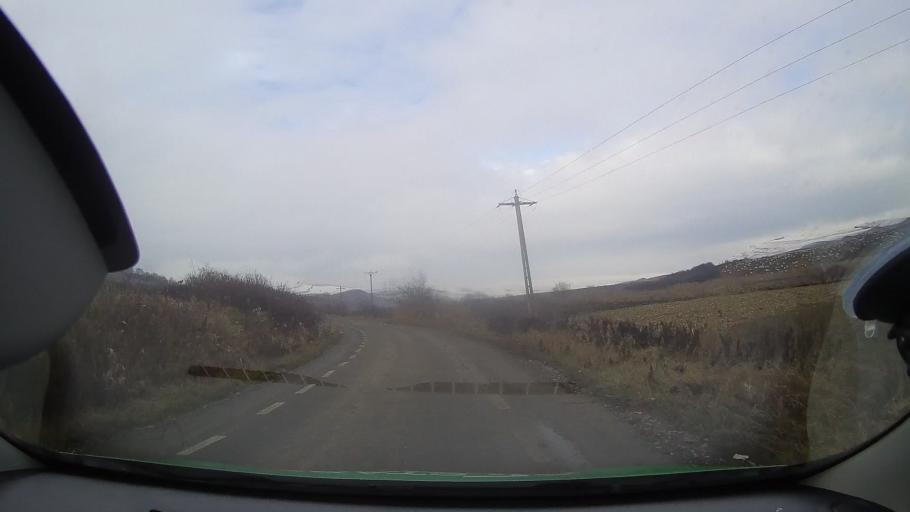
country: RO
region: Mures
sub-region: Comuna Atintis
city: Atintis
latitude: 46.4070
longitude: 24.0863
